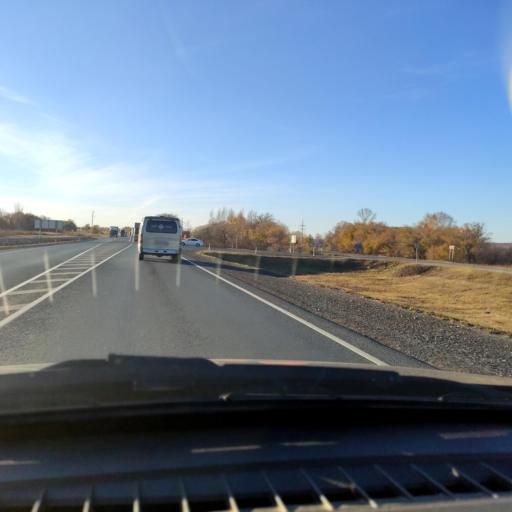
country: RU
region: Samara
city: Varlamovo
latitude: 53.1945
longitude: 48.3261
